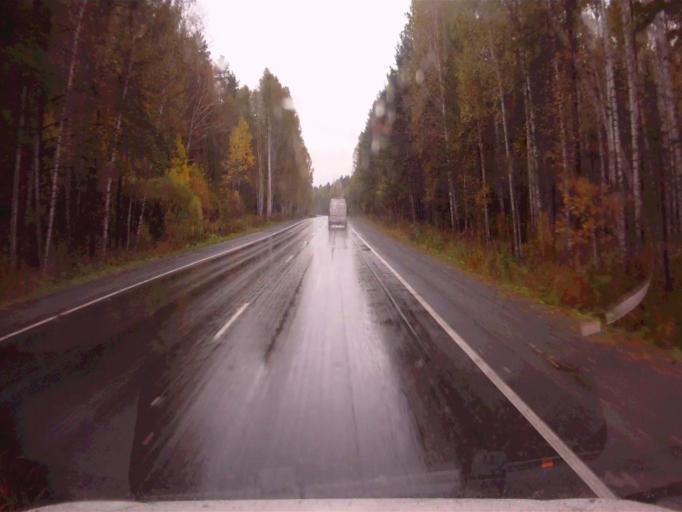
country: RU
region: Chelyabinsk
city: Tayginka
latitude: 55.5652
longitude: 60.6496
